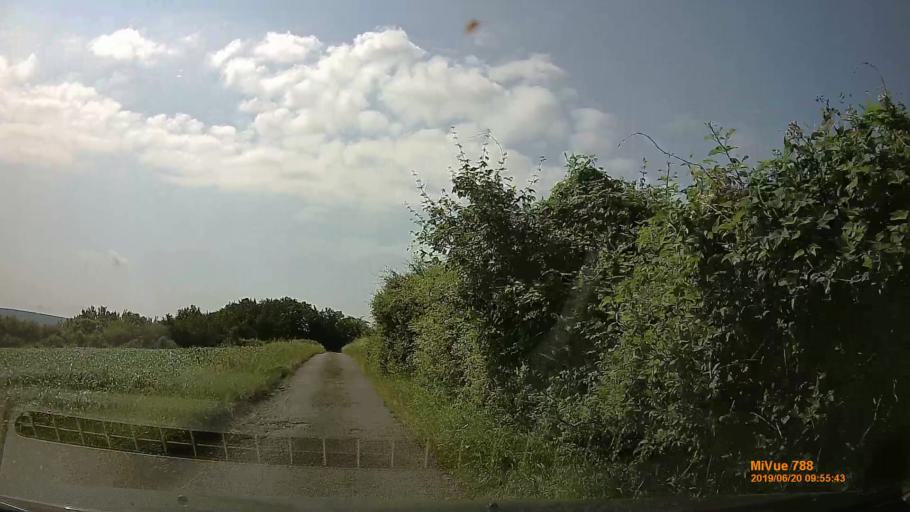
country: HU
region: Baranya
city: Pecsvarad
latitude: 46.1708
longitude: 18.4689
